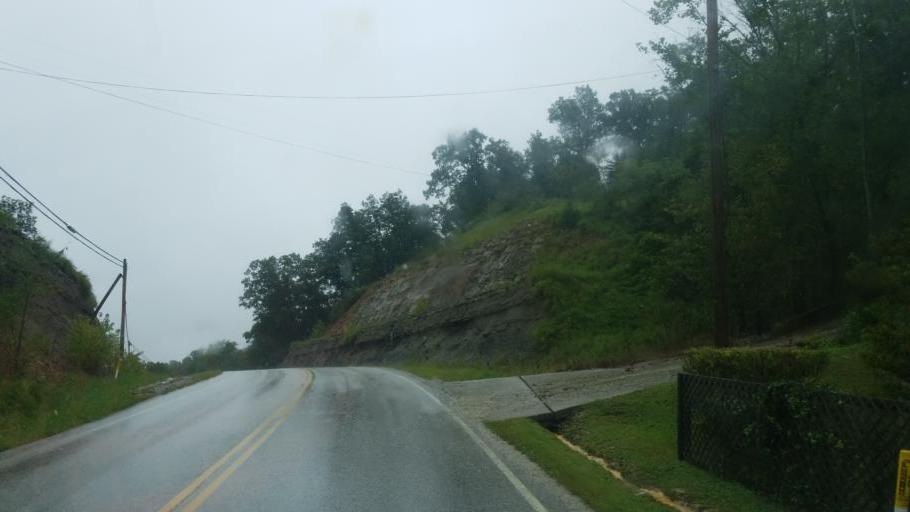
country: US
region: Kentucky
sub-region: Greenup County
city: South Shore
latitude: 38.7134
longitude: -82.9550
